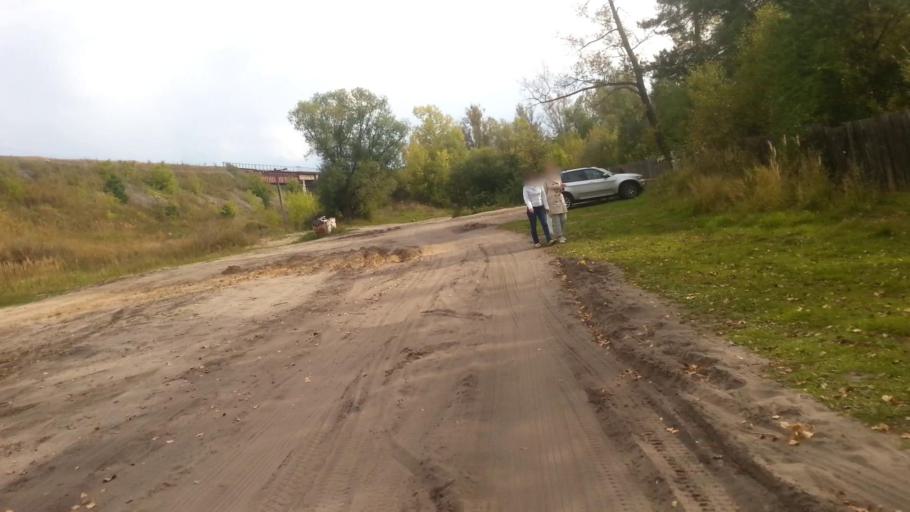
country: RU
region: Altai Krai
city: Yuzhnyy
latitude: 53.3078
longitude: 83.7001
